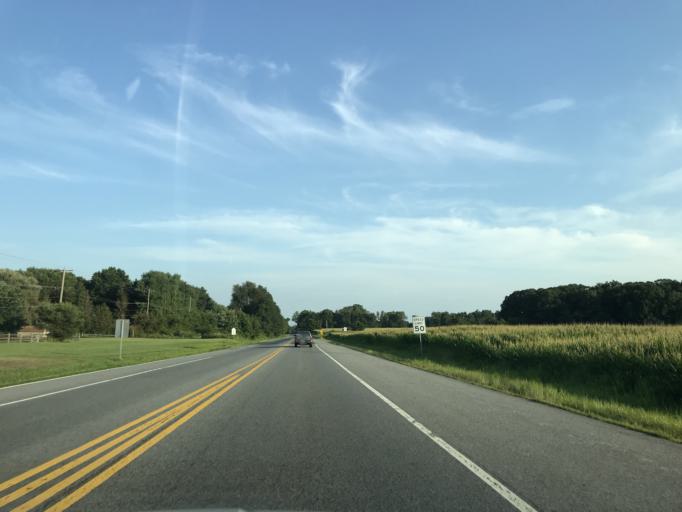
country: US
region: Maryland
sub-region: Cecil County
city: Rising Sun
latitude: 39.6879
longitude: -75.9726
